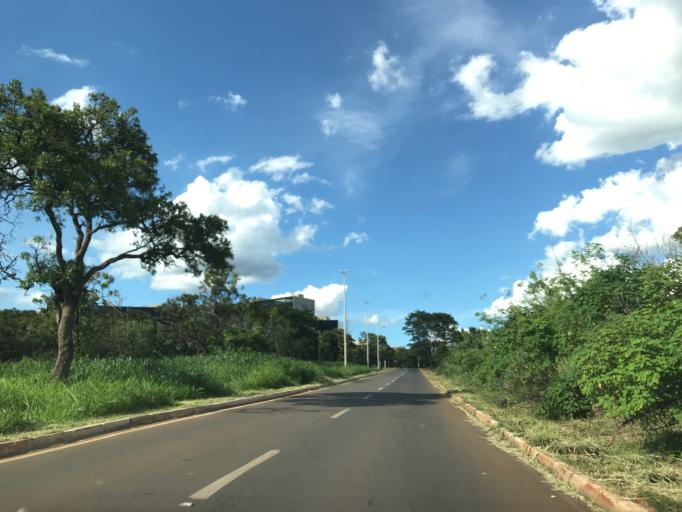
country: BR
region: Federal District
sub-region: Brasilia
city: Brasilia
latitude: -15.8155
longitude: -47.8680
